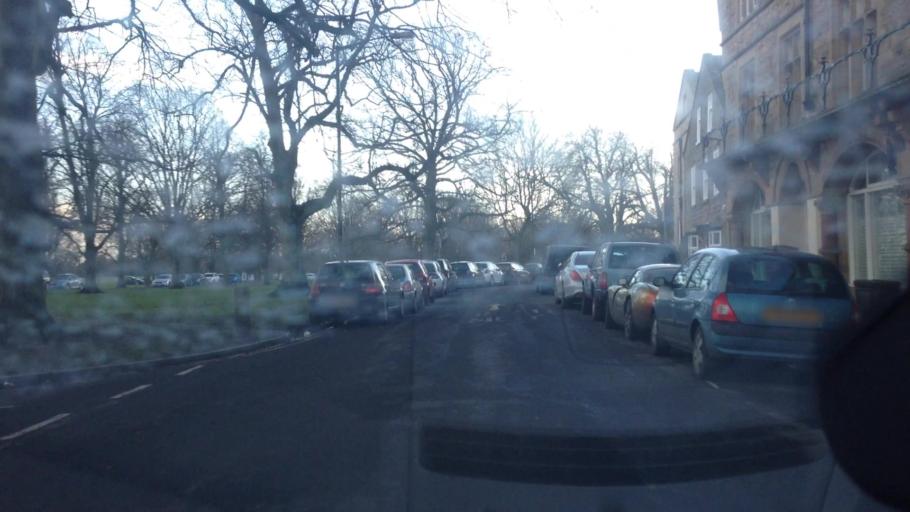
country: GB
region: England
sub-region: North Yorkshire
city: Harrogate
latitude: 53.9950
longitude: -1.5274
